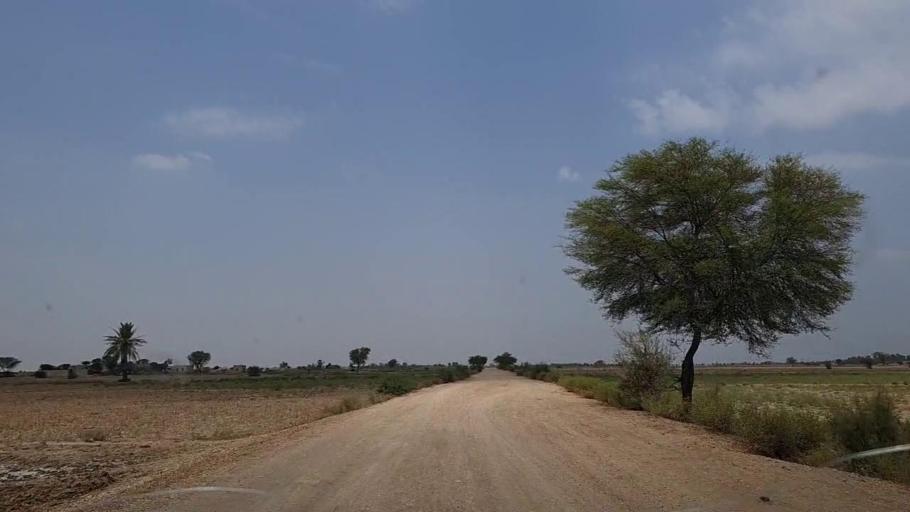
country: PK
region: Sindh
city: Phulji
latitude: 26.8038
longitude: 67.6340
